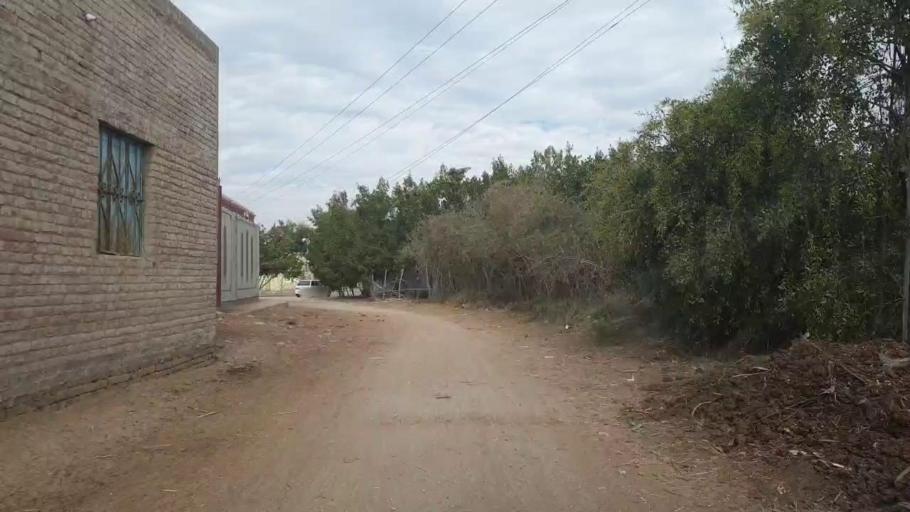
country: PK
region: Sindh
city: Sinjhoro
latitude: 26.0273
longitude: 68.8743
